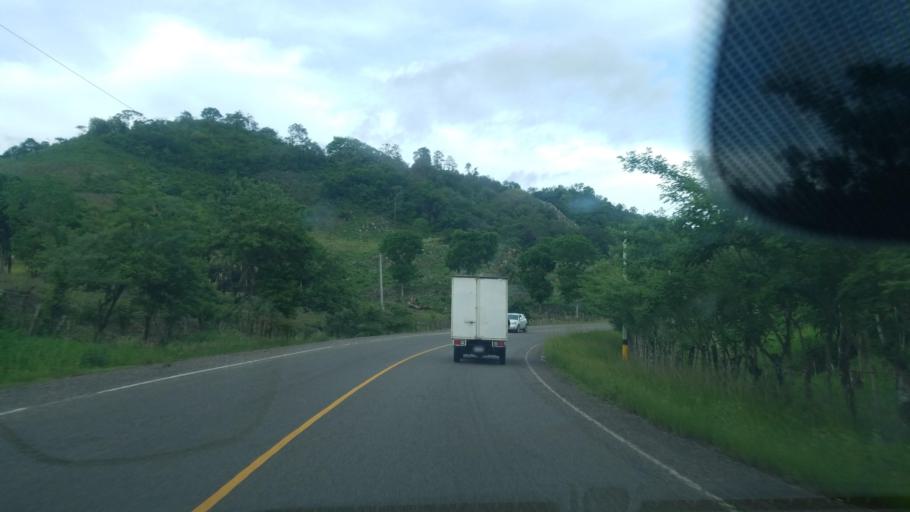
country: HN
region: Santa Barbara
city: Concepcion del Sur
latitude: 14.8079
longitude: -88.1791
